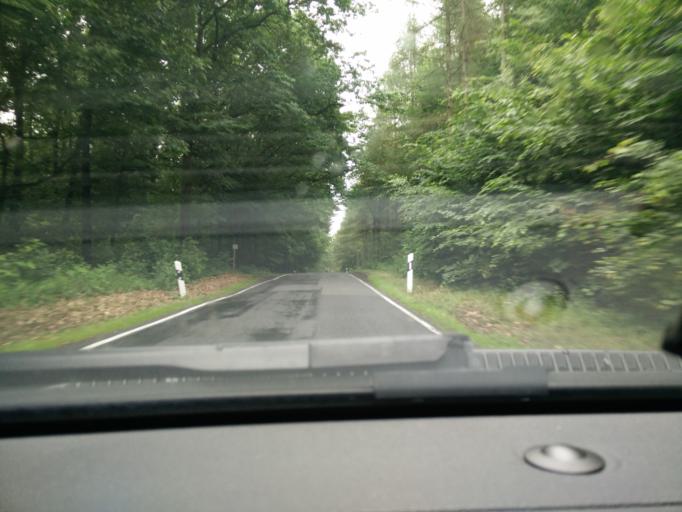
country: DE
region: Saxony
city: Grossbardau
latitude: 51.1680
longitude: 12.7007
